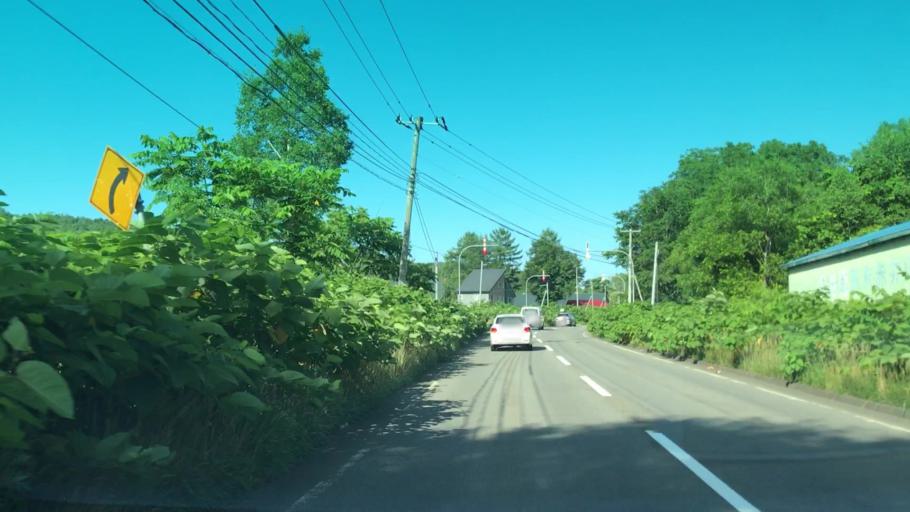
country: JP
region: Hokkaido
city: Otaru
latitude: 43.0857
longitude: 140.9172
